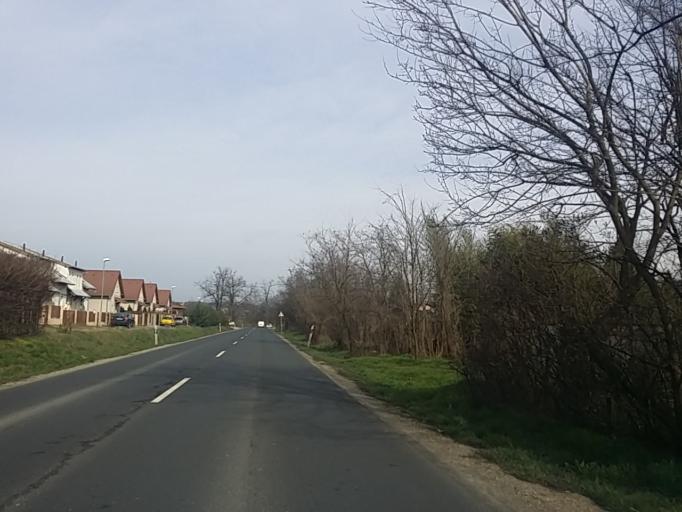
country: HU
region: Pest
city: Fot
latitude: 47.6225
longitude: 19.1986
